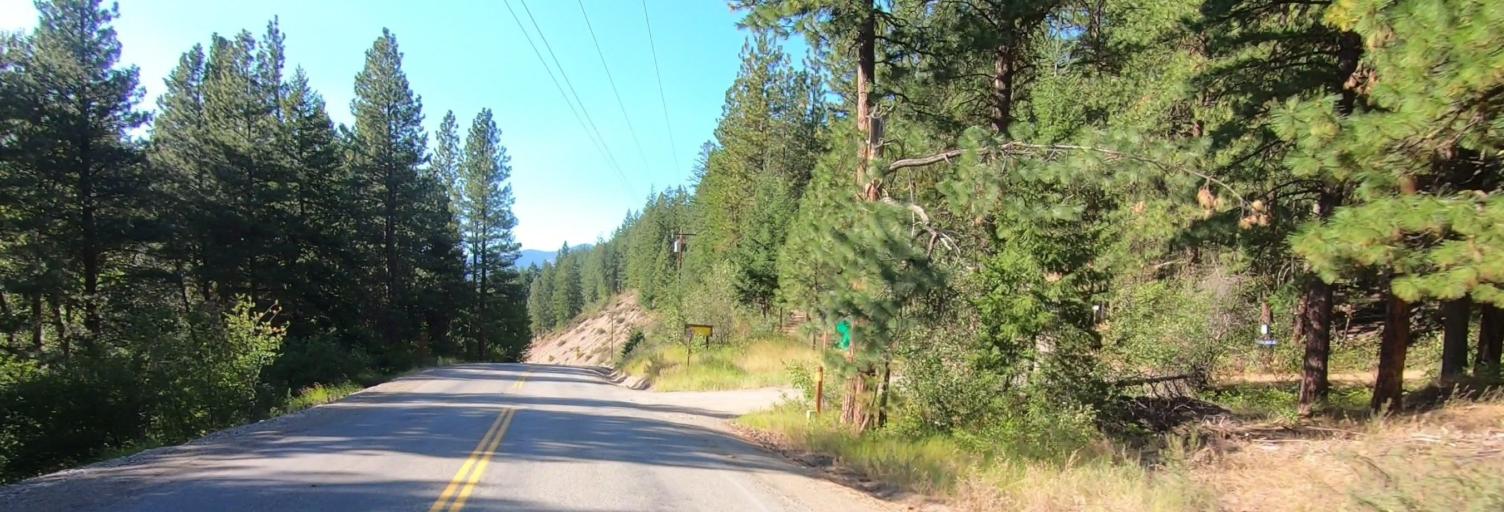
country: US
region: Washington
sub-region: Chelan County
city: Granite Falls
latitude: 48.5477
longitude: -120.3264
